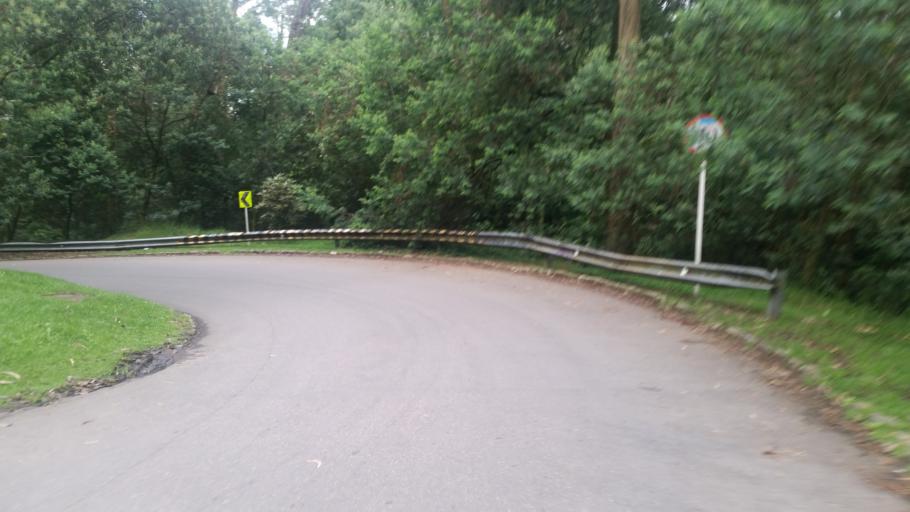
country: CO
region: Bogota D.C.
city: Bogota
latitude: 4.6237
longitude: -74.0591
